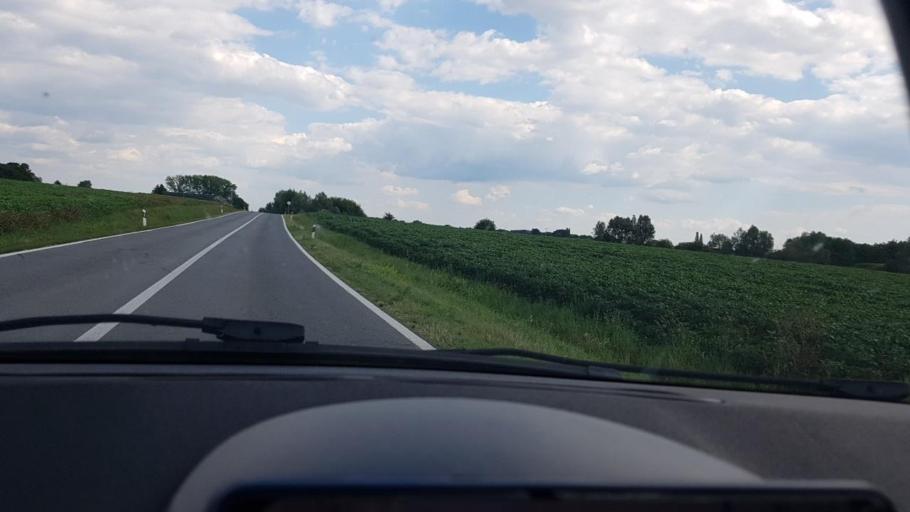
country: HR
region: Bjelovarsko-Bilogorska
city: Zdralovi
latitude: 45.8420
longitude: 16.9502
